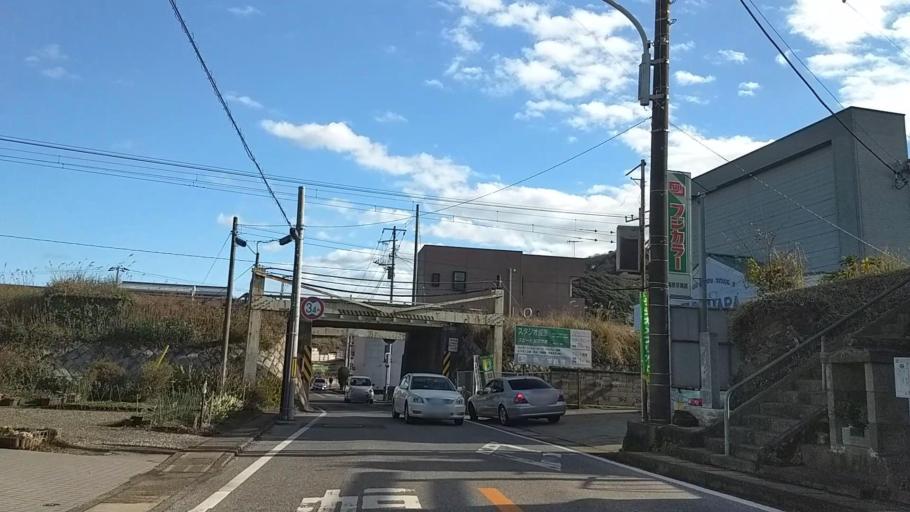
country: JP
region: Chiba
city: Tateyama
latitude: 35.0269
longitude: 139.8524
